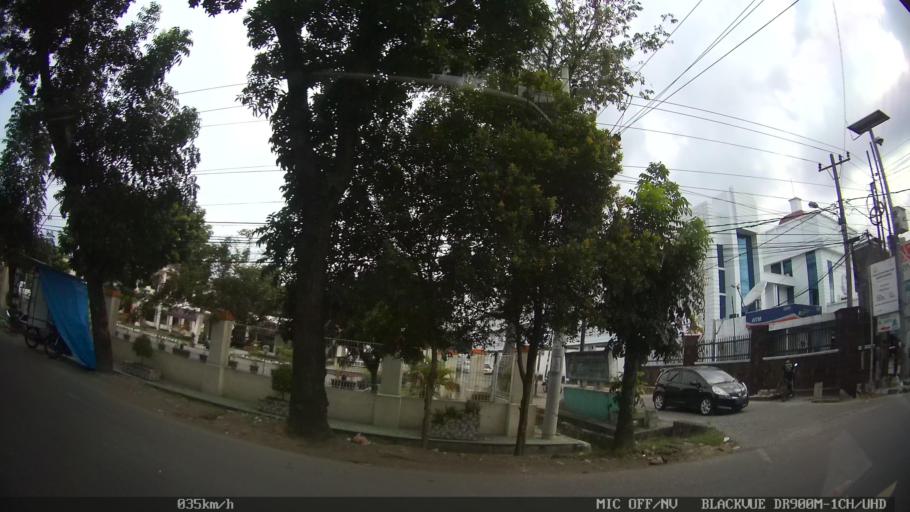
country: ID
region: North Sumatra
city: Deli Tua
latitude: 3.5415
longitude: 98.6771
